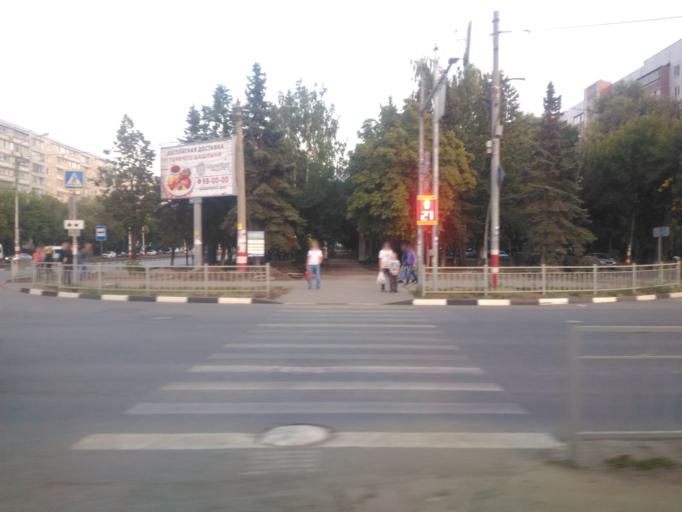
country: RU
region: Ulyanovsk
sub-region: Ulyanovskiy Rayon
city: Ulyanovsk
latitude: 54.2754
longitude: 48.2906
